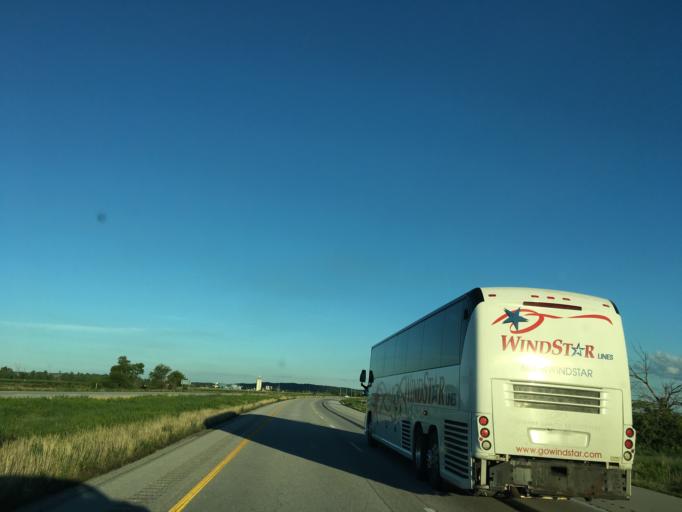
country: US
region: Iowa
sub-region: Fremont County
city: Hamburg
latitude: 40.6090
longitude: -95.6864
